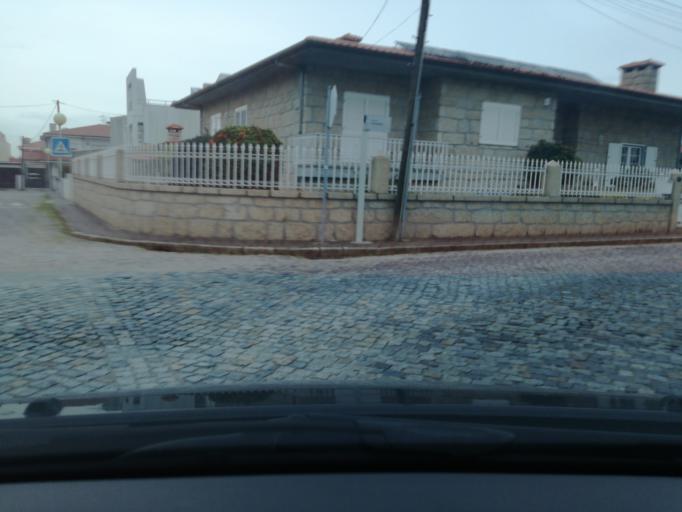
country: PT
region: Porto
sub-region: Maia
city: Gemunde
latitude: 41.2580
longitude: -8.6685
